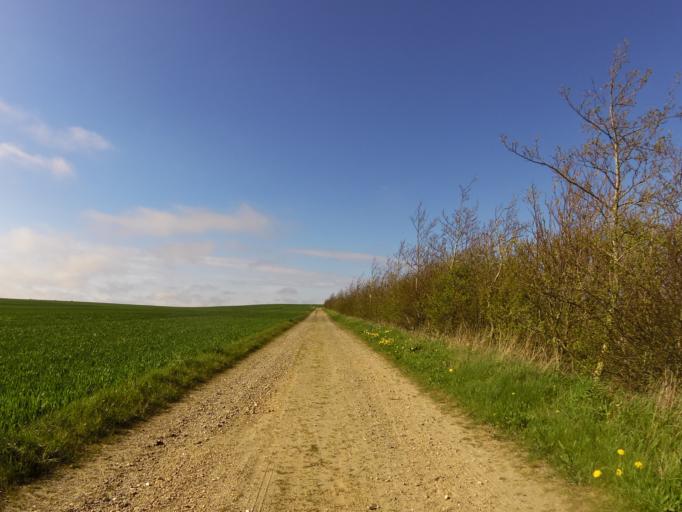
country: DK
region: South Denmark
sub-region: Tonder Kommune
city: Sherrebek
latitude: 55.1553
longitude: 8.8018
